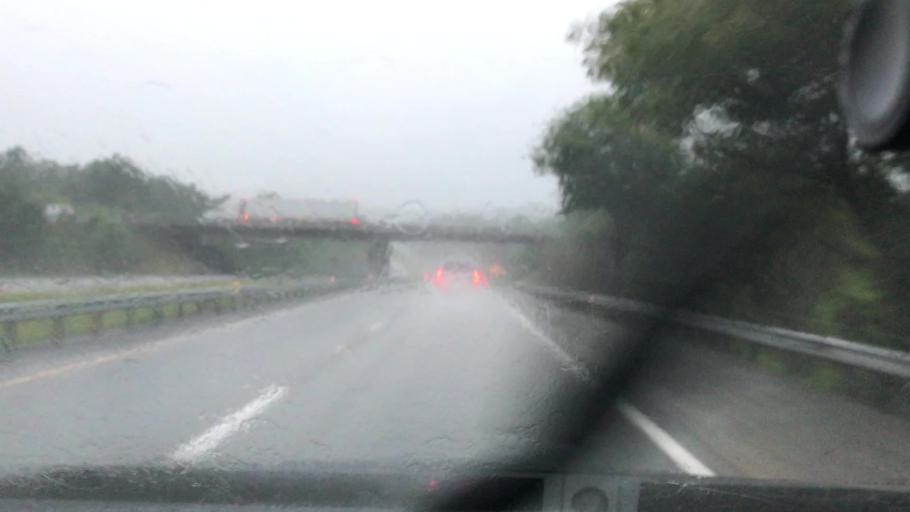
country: US
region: Virginia
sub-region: Giles County
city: Pearisburg
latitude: 37.3356
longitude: -80.7398
